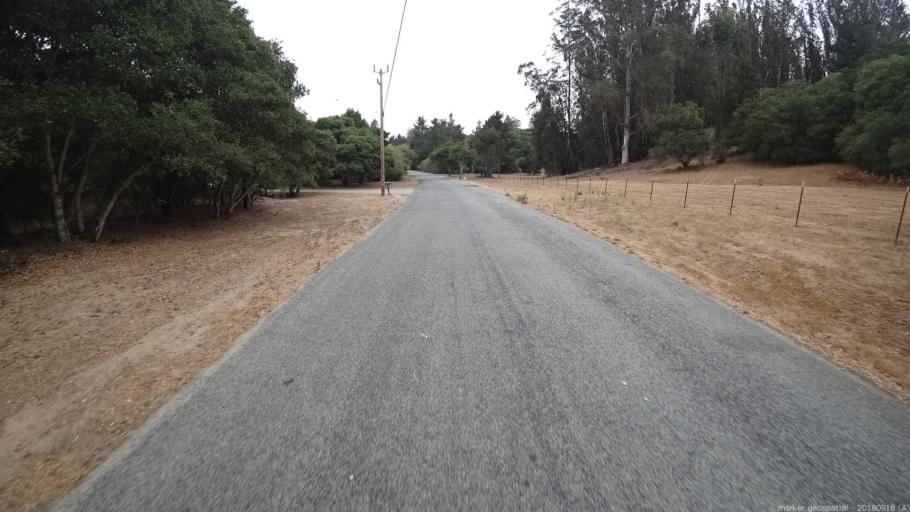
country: US
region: California
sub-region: Monterey County
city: Prunedale
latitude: 36.7833
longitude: -121.6414
